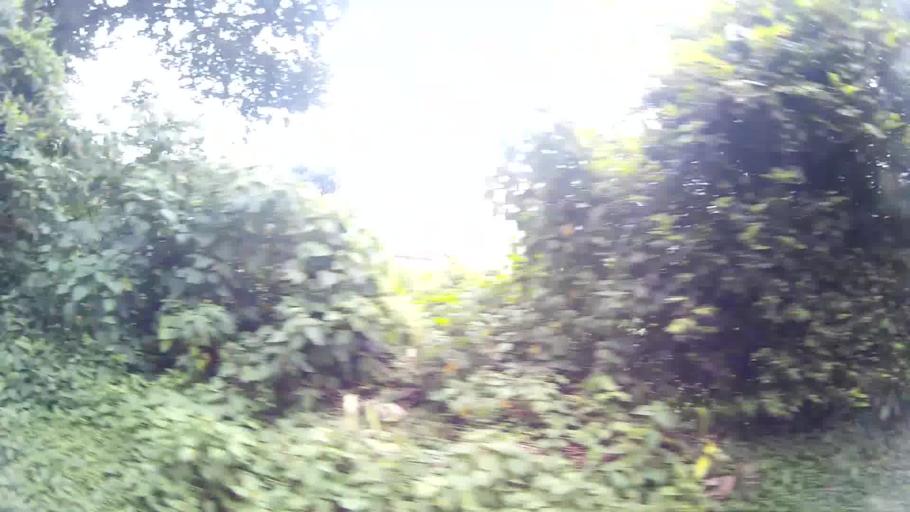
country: CO
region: Risaralda
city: Pereira
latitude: 4.7683
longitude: -75.7189
